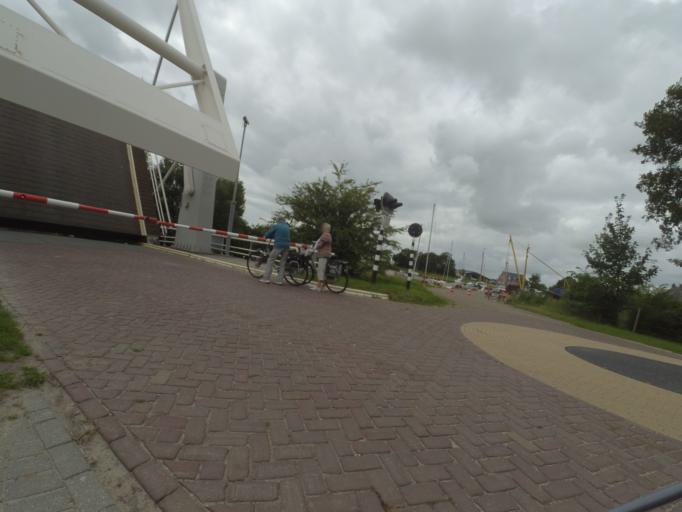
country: NL
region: Friesland
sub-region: Gemeente Dongeradeel
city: Anjum
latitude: 53.3228
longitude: 6.1023
